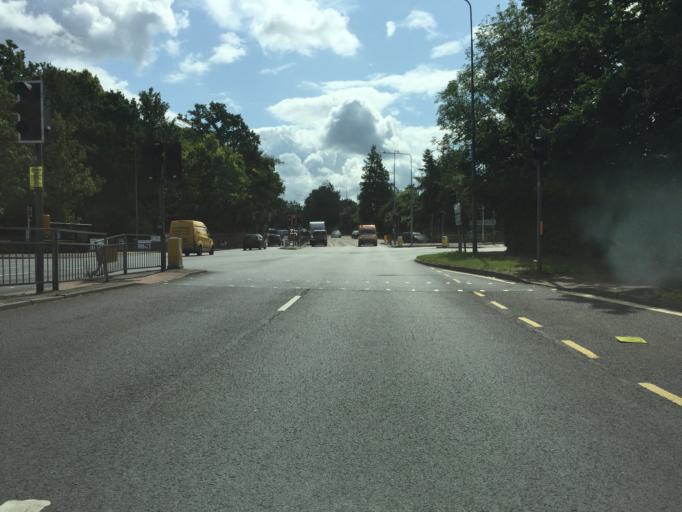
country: GB
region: England
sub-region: Kent
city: Aylesford
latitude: 51.2943
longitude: 0.4713
